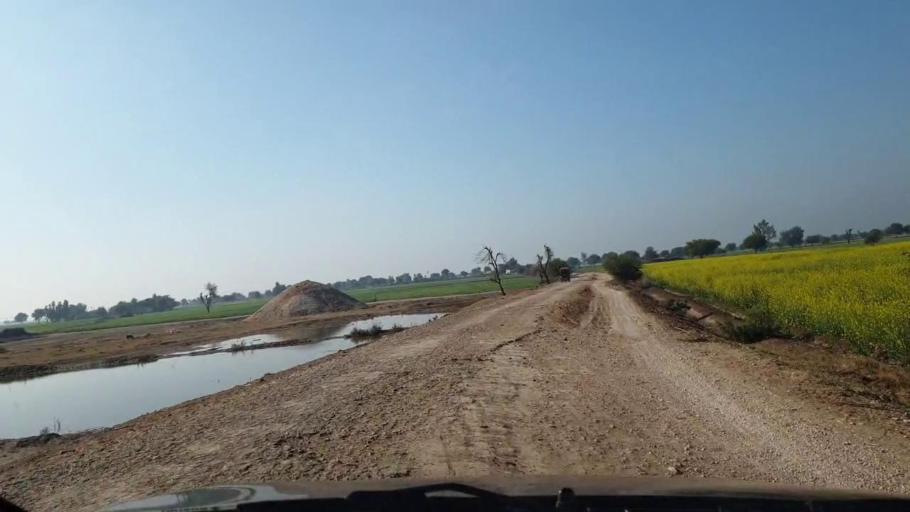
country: PK
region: Sindh
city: Sinjhoro
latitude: 25.9934
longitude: 68.7530
